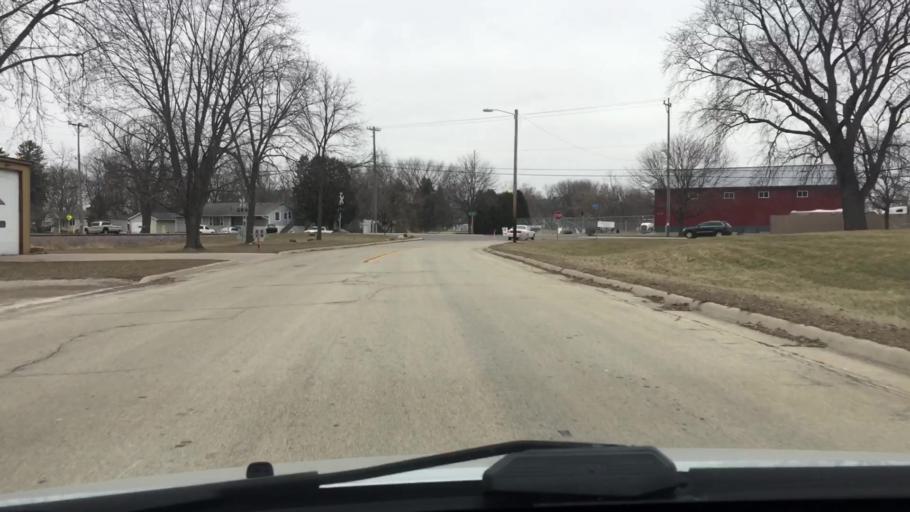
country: US
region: Wisconsin
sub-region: Jefferson County
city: Watertown
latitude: 43.1885
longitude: -88.7339
